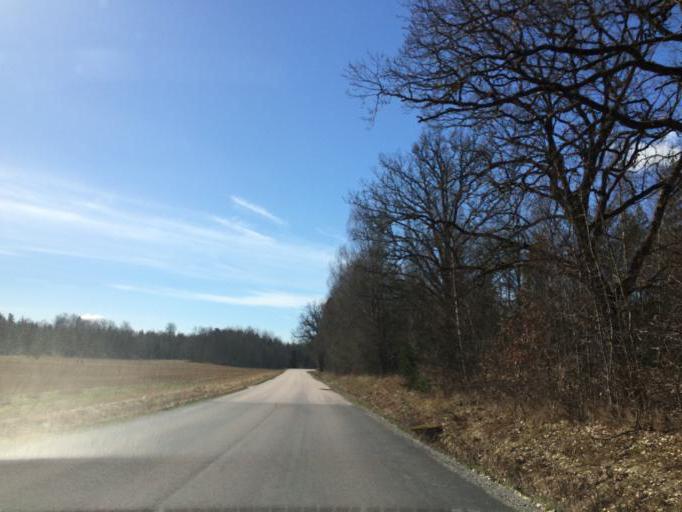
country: SE
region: Vaestmanland
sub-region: Hallstahammars Kommun
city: Kolback
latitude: 59.5288
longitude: 16.3169
